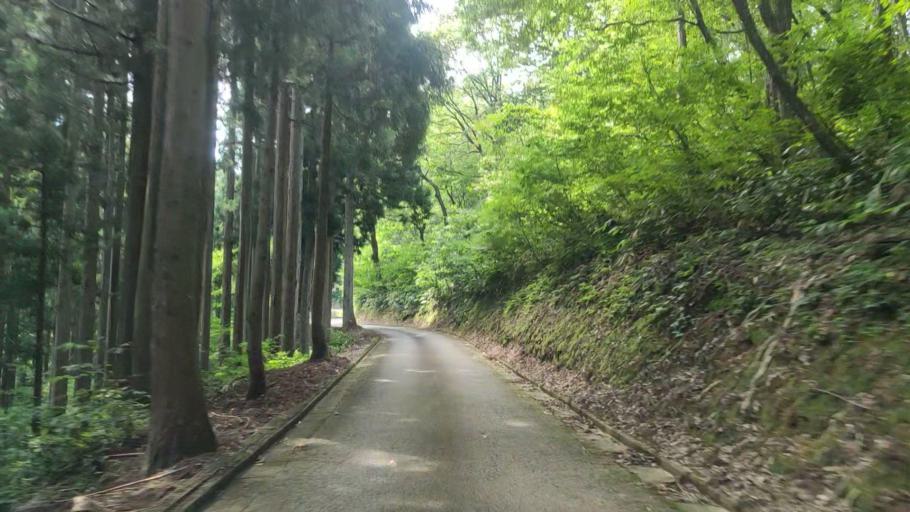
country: JP
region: Ishikawa
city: Komatsu
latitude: 36.2817
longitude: 136.5300
